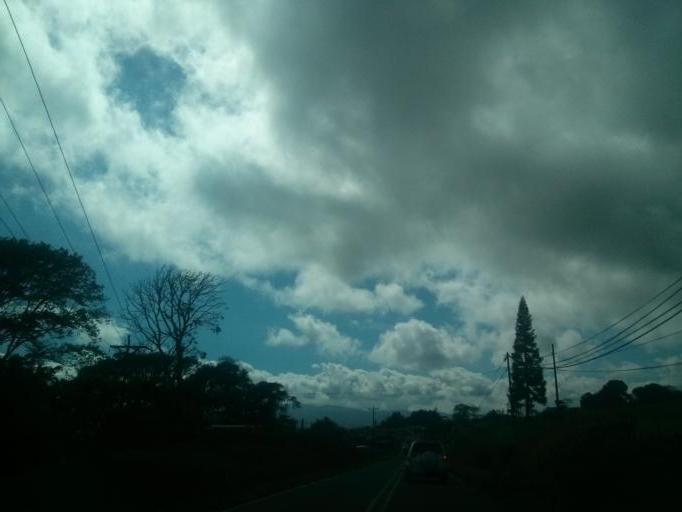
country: CR
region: Cartago
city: Cot
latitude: 9.8891
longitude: -83.8596
